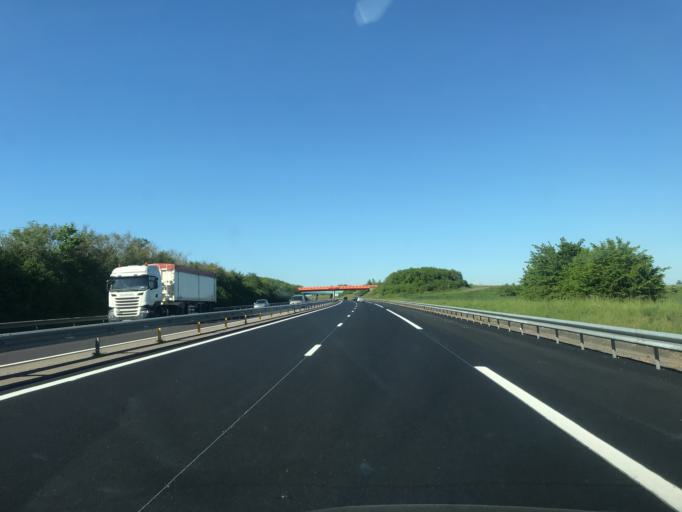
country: FR
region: Haute-Normandie
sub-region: Departement de l'Eure
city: Evreux
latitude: 48.9230
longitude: 1.2030
